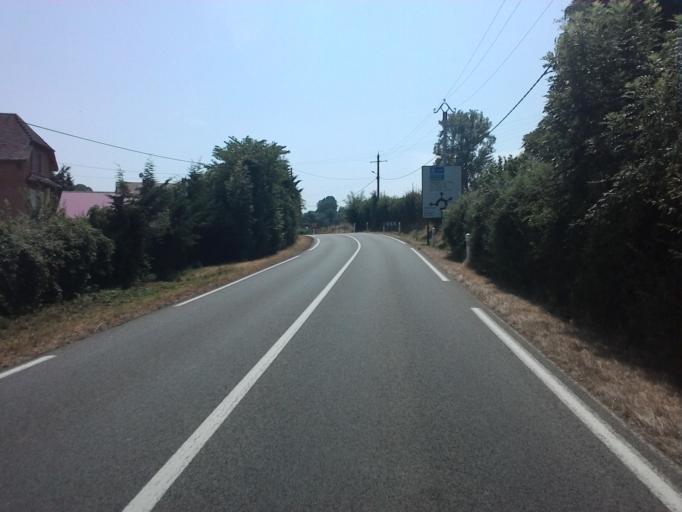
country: FR
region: Rhone-Alpes
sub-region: Departement de l'Isere
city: Corbelin
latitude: 45.6119
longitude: 5.5375
